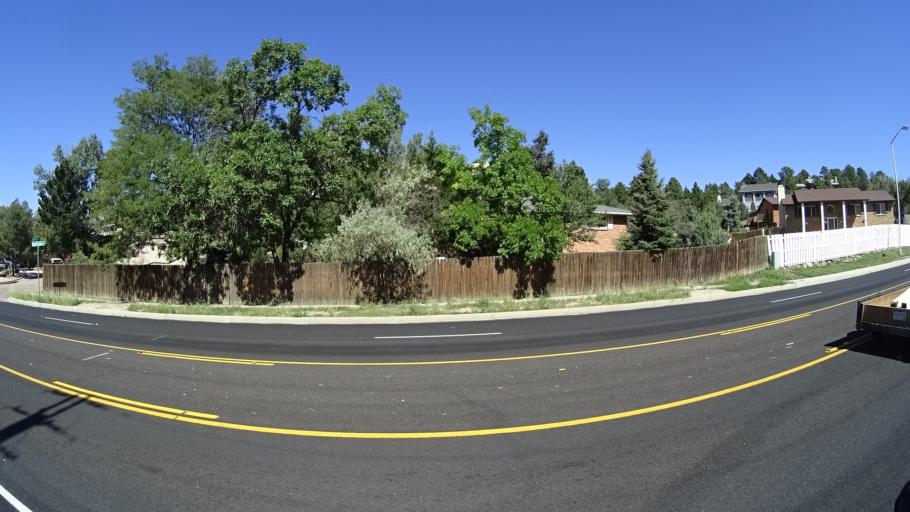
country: US
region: Colorado
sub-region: El Paso County
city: Cimarron Hills
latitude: 38.8635
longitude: -104.7445
